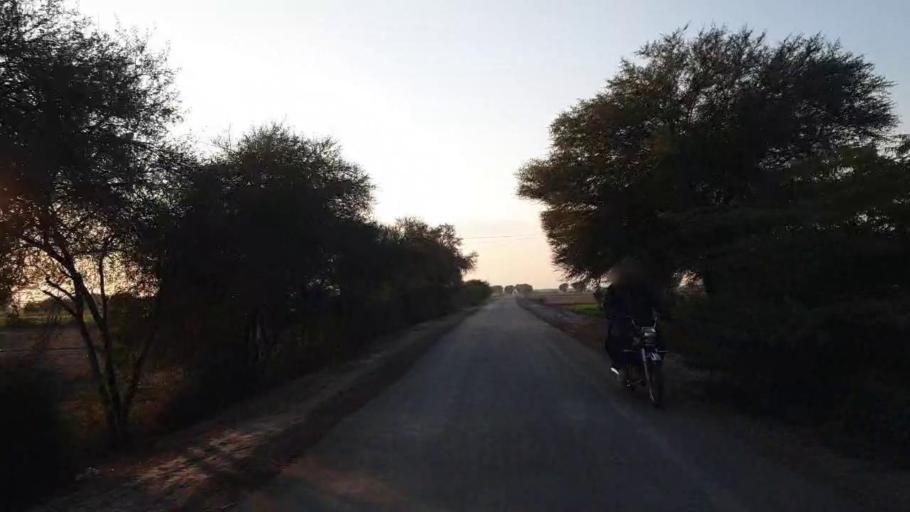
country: PK
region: Sindh
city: Shahpur Chakar
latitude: 26.1554
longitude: 68.5596
